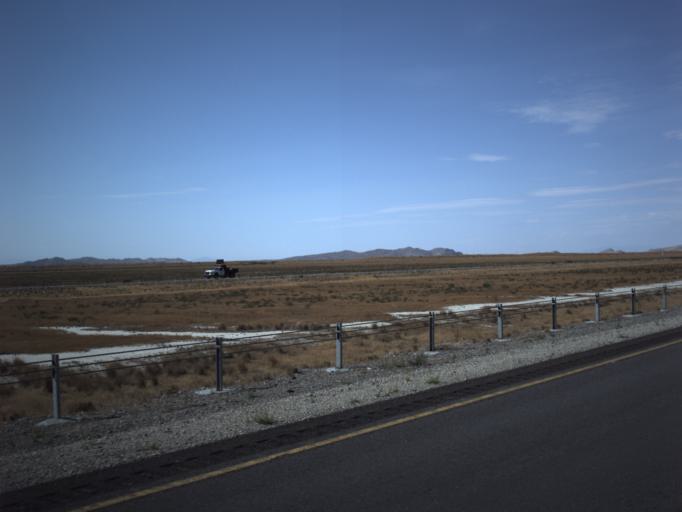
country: US
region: Utah
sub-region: Tooele County
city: Grantsville
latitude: 40.7265
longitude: -113.1835
